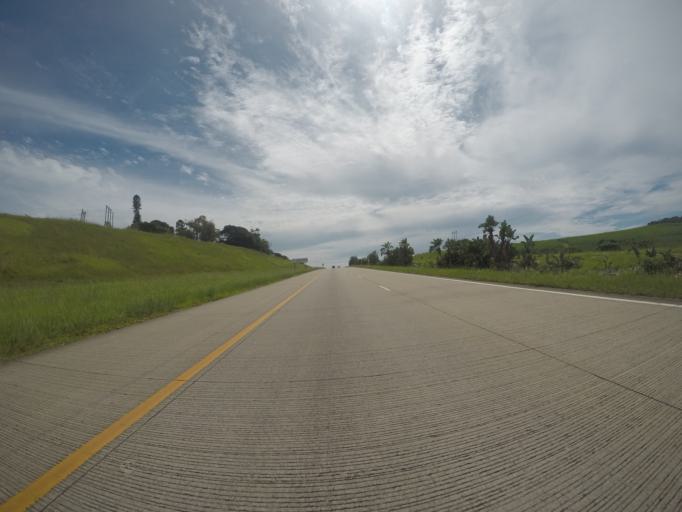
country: ZA
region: KwaZulu-Natal
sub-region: iLembe District Municipality
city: Stanger
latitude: -29.3450
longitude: 31.3251
